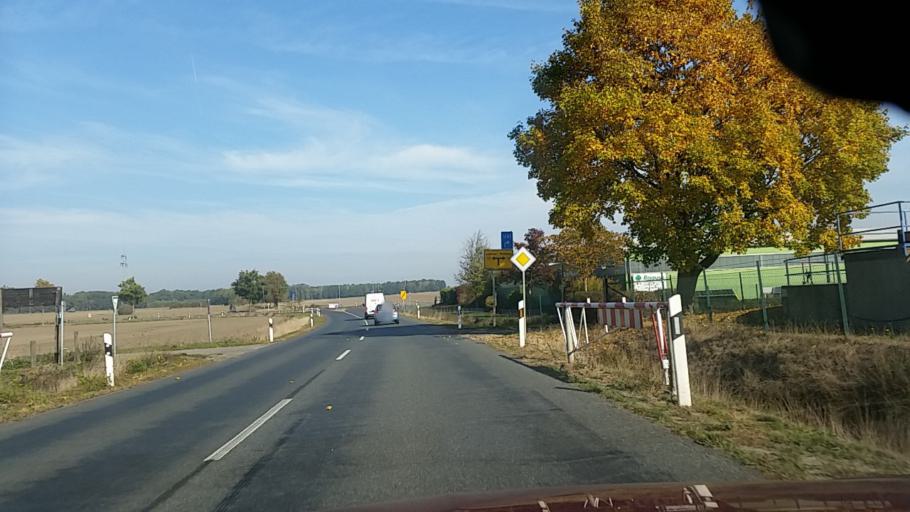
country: DE
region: Lower Saxony
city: Weyhausen
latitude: 52.4636
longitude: 10.7081
